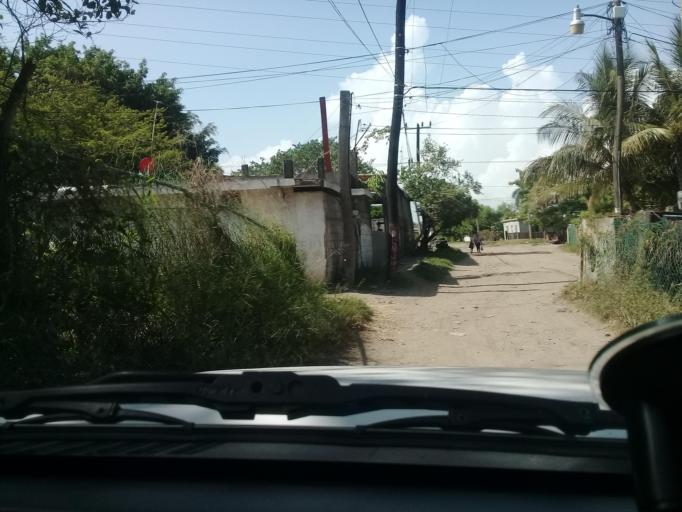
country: MX
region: Veracruz
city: Moralillo
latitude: 22.2266
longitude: -97.9031
